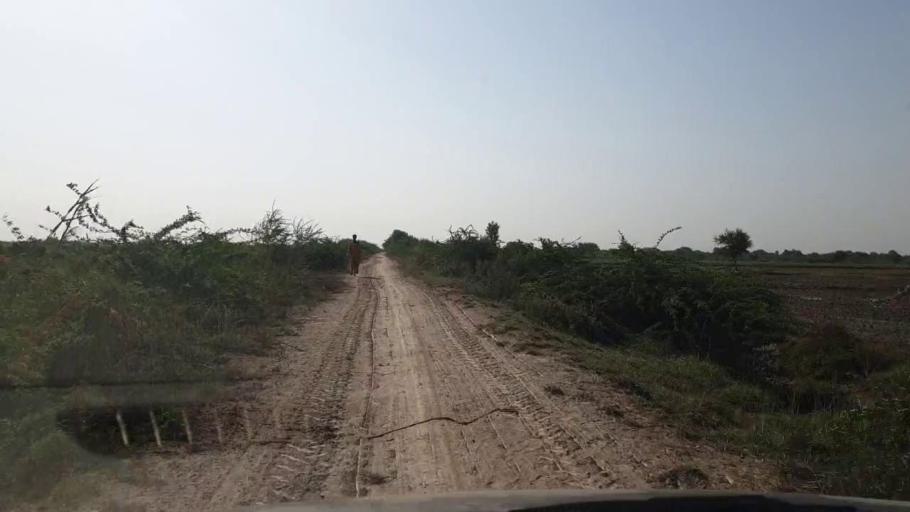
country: PK
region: Sindh
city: Kadhan
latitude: 24.5897
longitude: 69.0770
